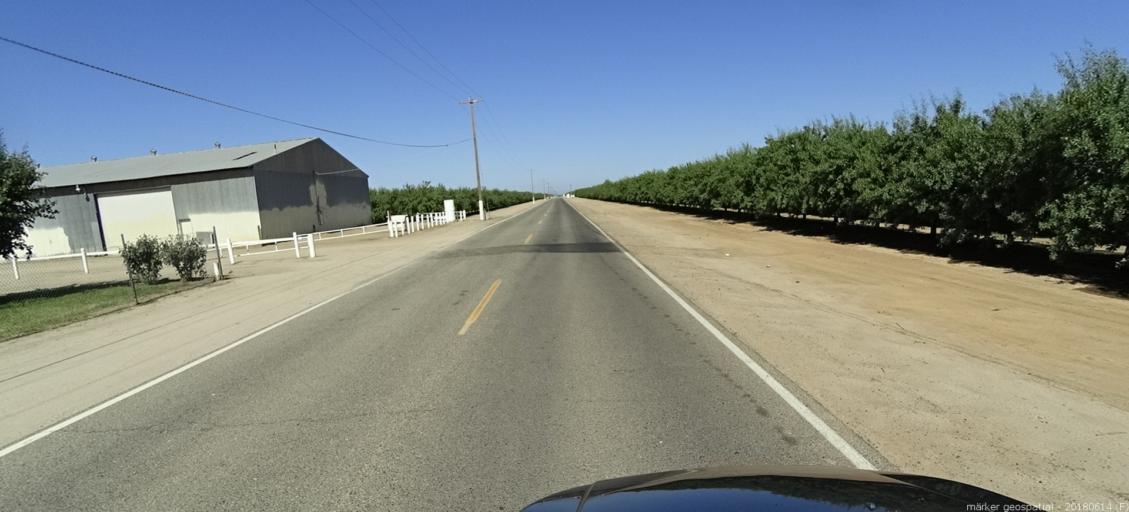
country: US
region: California
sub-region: Madera County
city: Madera
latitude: 36.9747
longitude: -120.1106
